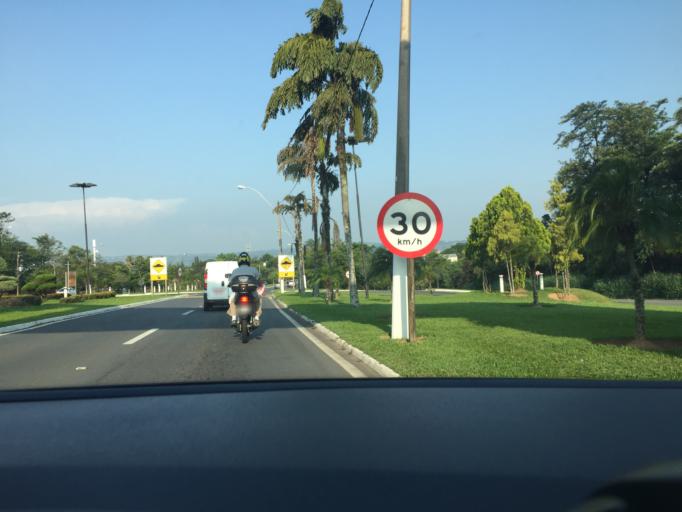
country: BR
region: Sao Paulo
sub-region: Valinhos
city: Valinhos
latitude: -23.0084
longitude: -47.0202
